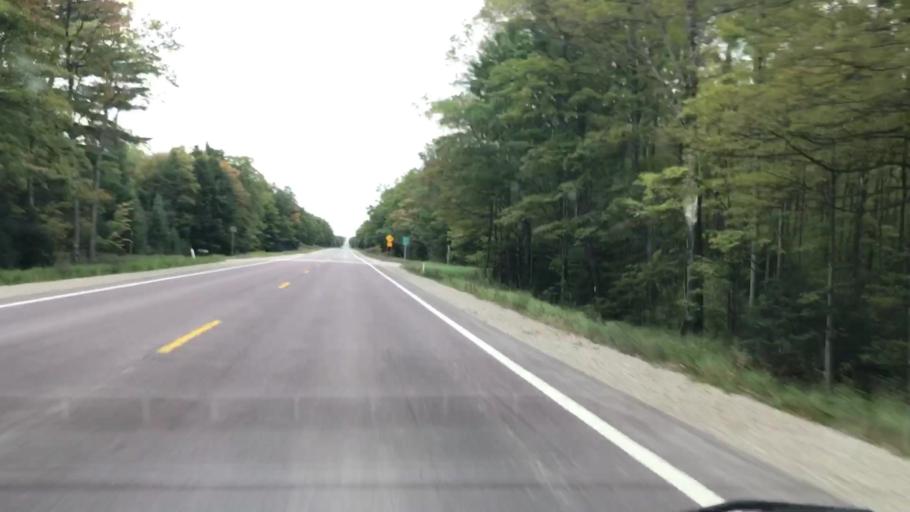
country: US
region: Michigan
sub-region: Luce County
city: Newberry
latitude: 46.2462
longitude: -85.5723
